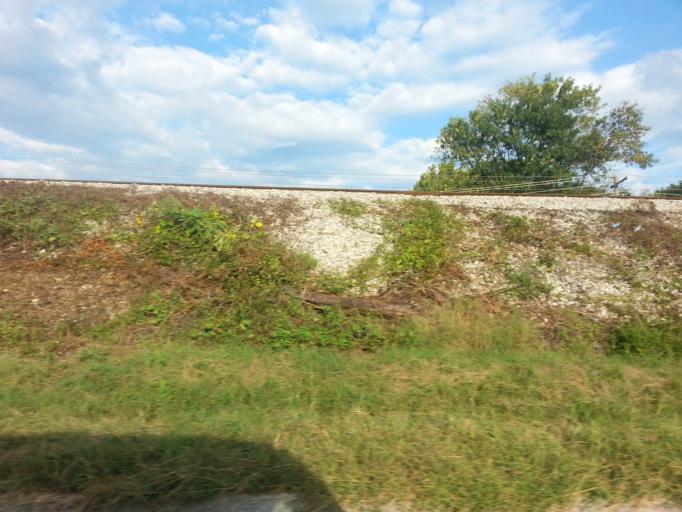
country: US
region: Tennessee
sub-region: Blount County
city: Alcoa
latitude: 35.7994
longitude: -83.9646
